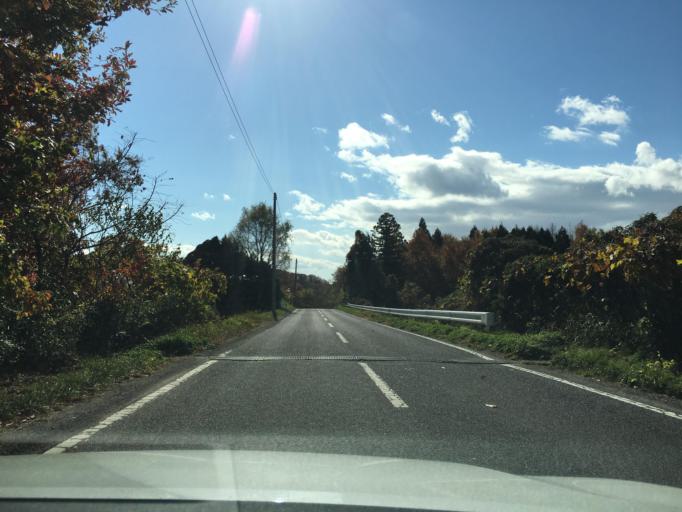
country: JP
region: Fukushima
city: Motomiya
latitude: 37.4750
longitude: 140.4254
